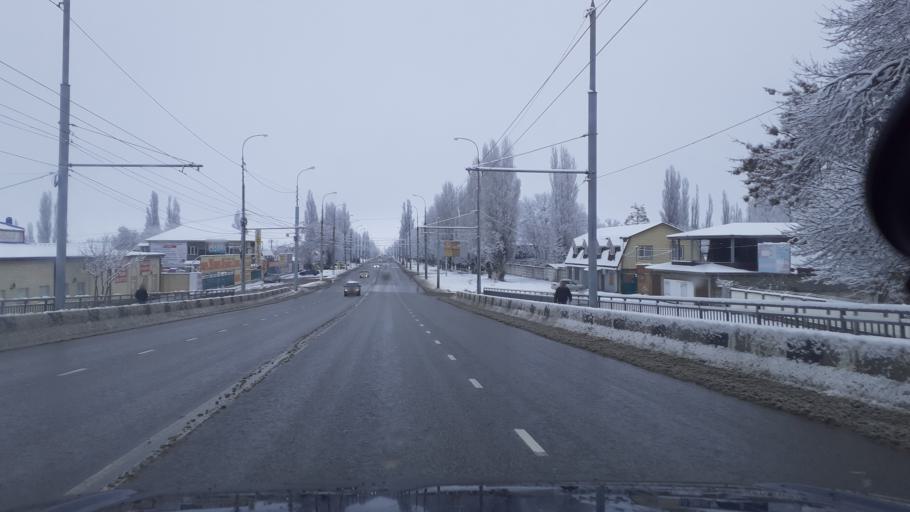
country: RU
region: Adygeya
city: Maykop
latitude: 44.6233
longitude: 40.1223
